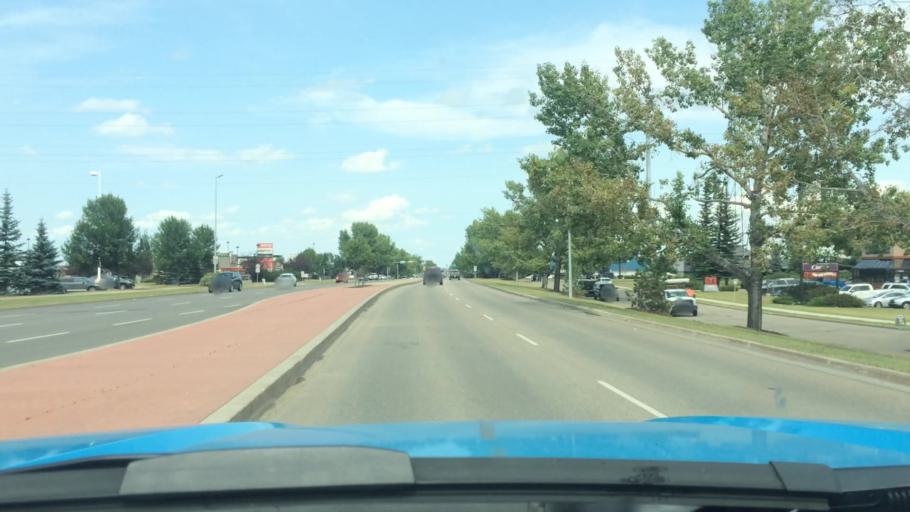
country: CA
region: Alberta
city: Red Deer
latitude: 52.2359
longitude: -113.8139
